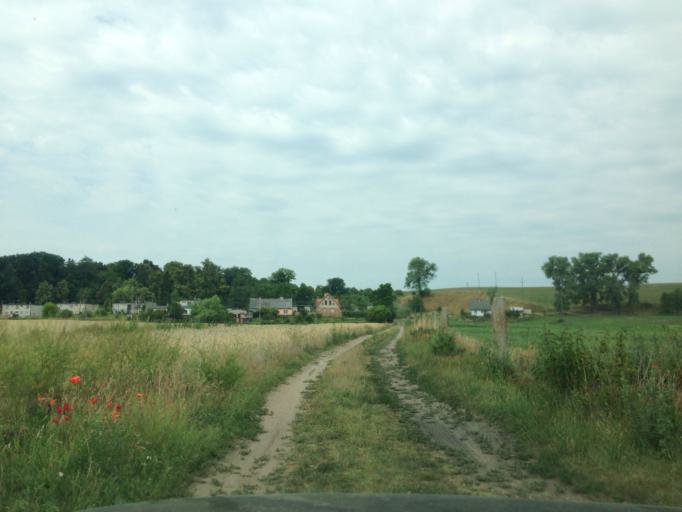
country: PL
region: Kujawsko-Pomorskie
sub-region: Powiat rypinski
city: Wapielsk
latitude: 53.2068
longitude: 19.2655
